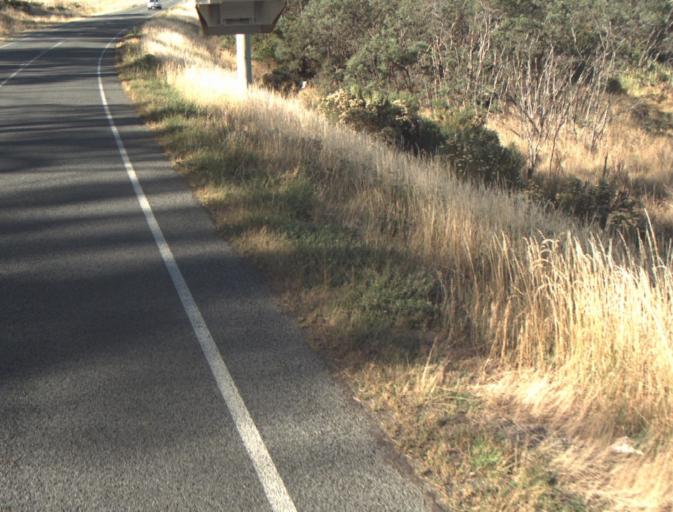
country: AU
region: Tasmania
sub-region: Launceston
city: Newstead
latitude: -41.4305
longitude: 147.2521
